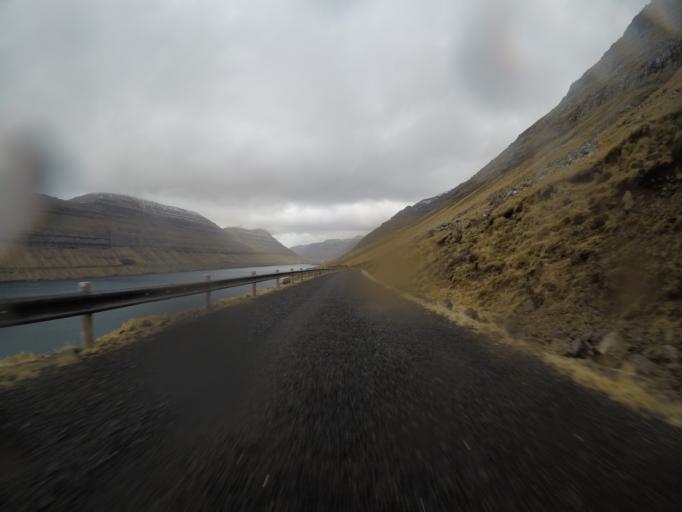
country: FO
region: Nordoyar
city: Klaksvik
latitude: 62.3283
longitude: -6.5686
